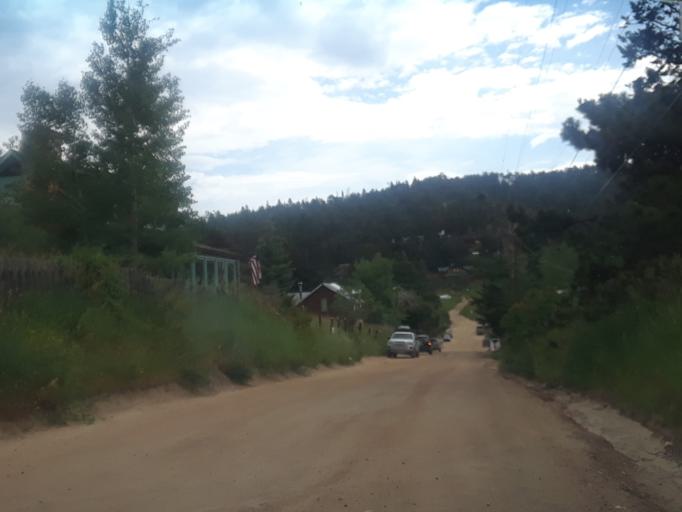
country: US
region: Colorado
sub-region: Boulder County
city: Nederland
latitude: 40.0633
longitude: -105.4111
